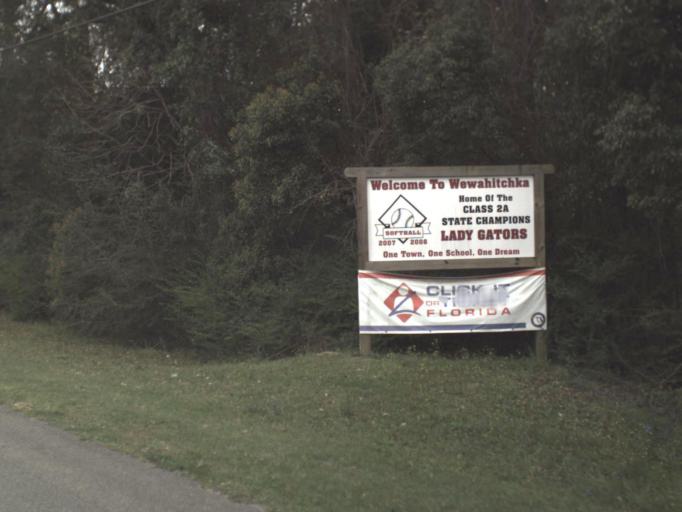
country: US
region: Florida
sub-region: Gulf County
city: Wewahitchka
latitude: 30.1207
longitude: -85.1990
